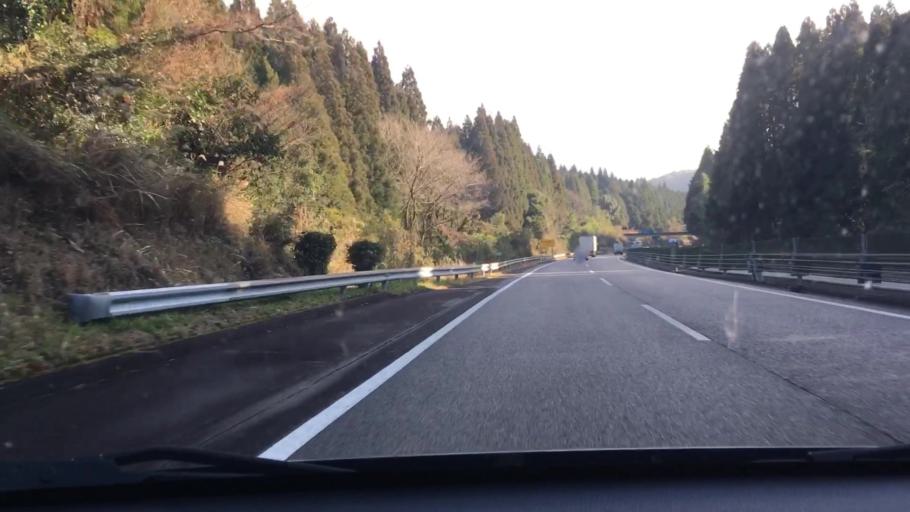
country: JP
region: Kagoshima
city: Okuchi-shinohara
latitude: 32.0008
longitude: 130.7578
